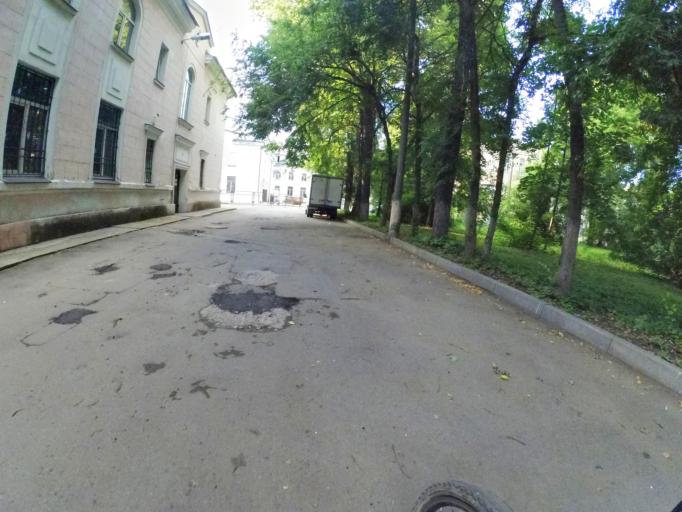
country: RU
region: Moscow
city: Strogino
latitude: 55.8338
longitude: 37.4264
